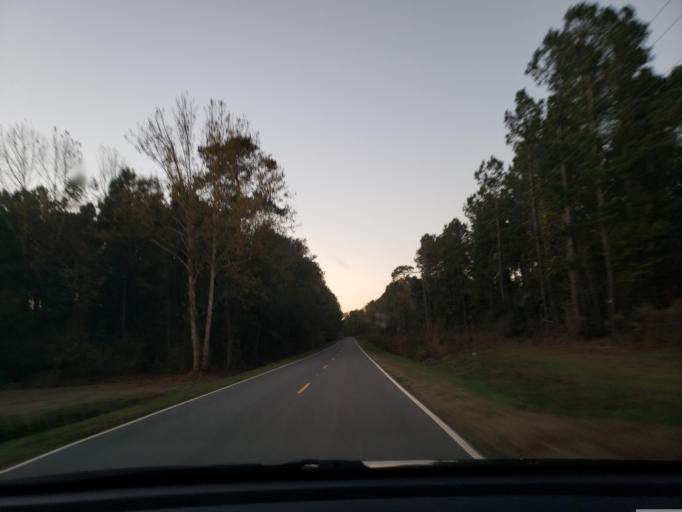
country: US
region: North Carolina
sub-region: Duplin County
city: Beulaville
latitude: 34.7845
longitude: -77.7555
